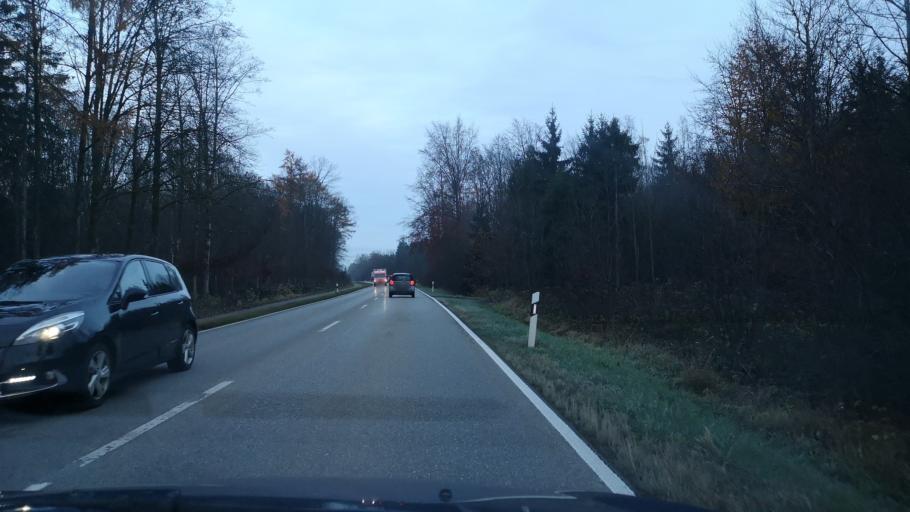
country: DE
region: Bavaria
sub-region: Upper Bavaria
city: Forstinning
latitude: 48.1513
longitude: 11.9131
